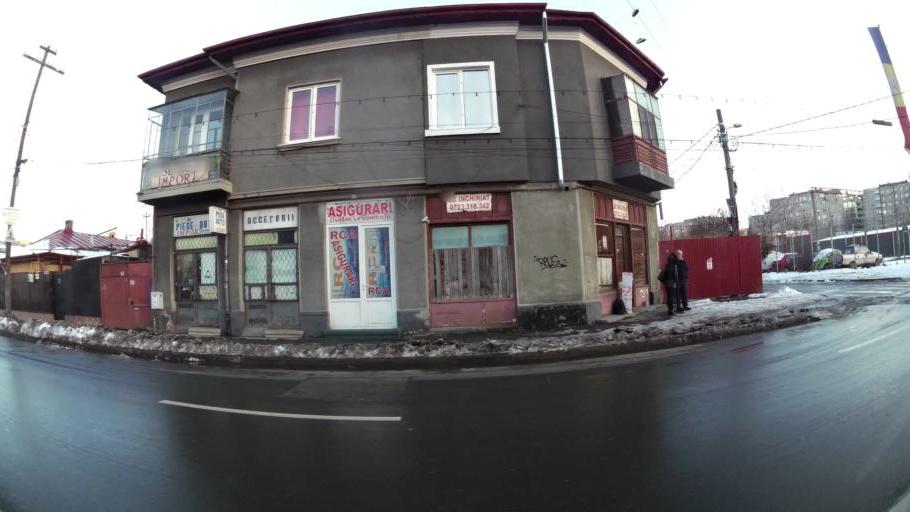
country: RO
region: Ilfov
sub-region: Comuna Fundeni-Dobroesti
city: Fundeni
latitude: 44.4477
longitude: 26.1452
